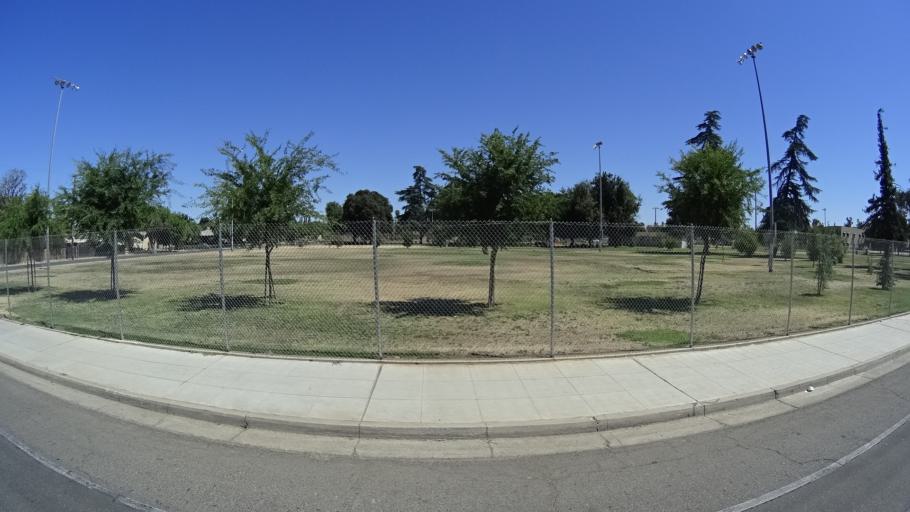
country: US
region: California
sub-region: Fresno County
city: Fresno
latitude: 36.7865
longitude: -119.8215
